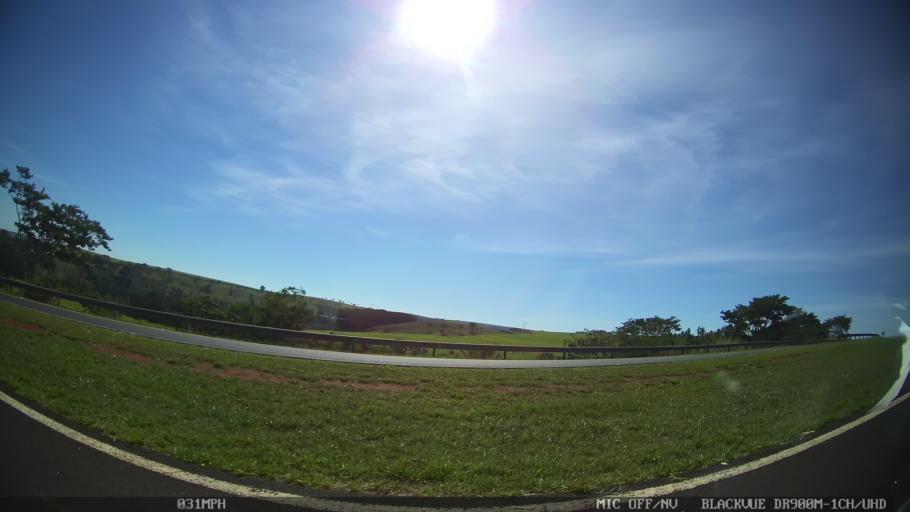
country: BR
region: Sao Paulo
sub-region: Santa Rita Do Passa Quatro
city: Santa Rita do Passa Quatro
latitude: -21.7545
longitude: -47.5642
